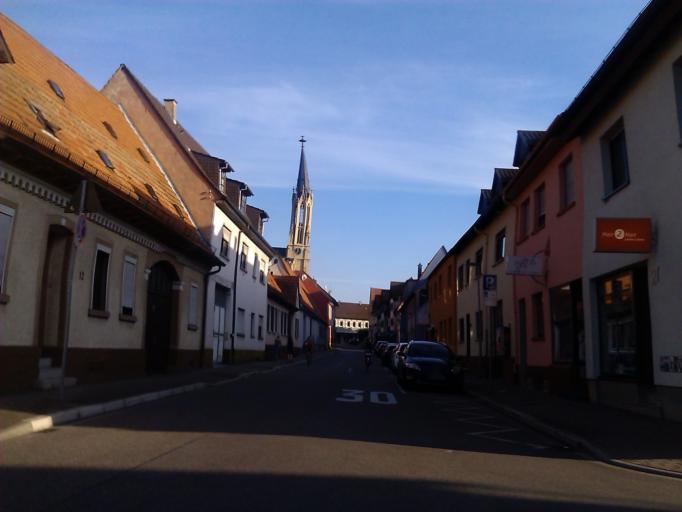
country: DE
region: Baden-Wuerttemberg
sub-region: Karlsruhe Region
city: Walldorf
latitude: 49.3048
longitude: 8.6421
